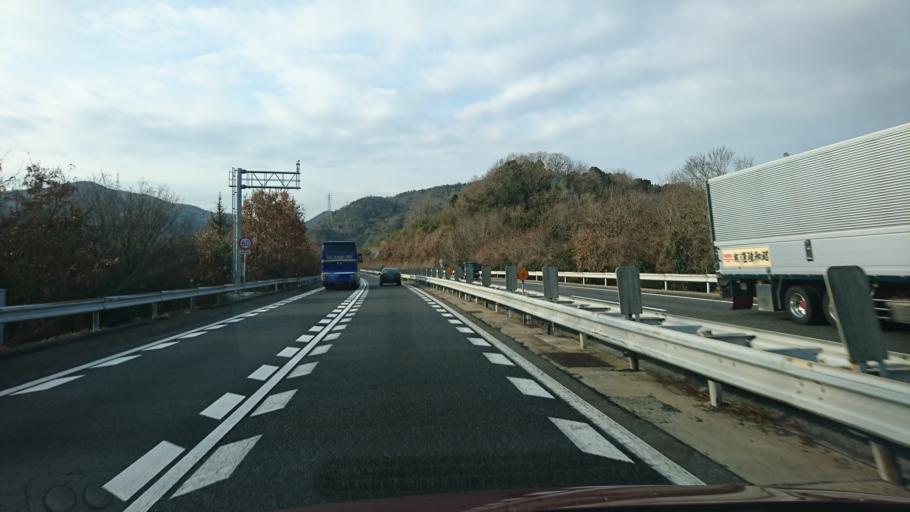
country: JP
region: Hyogo
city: Aioi
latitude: 34.8037
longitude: 134.4386
